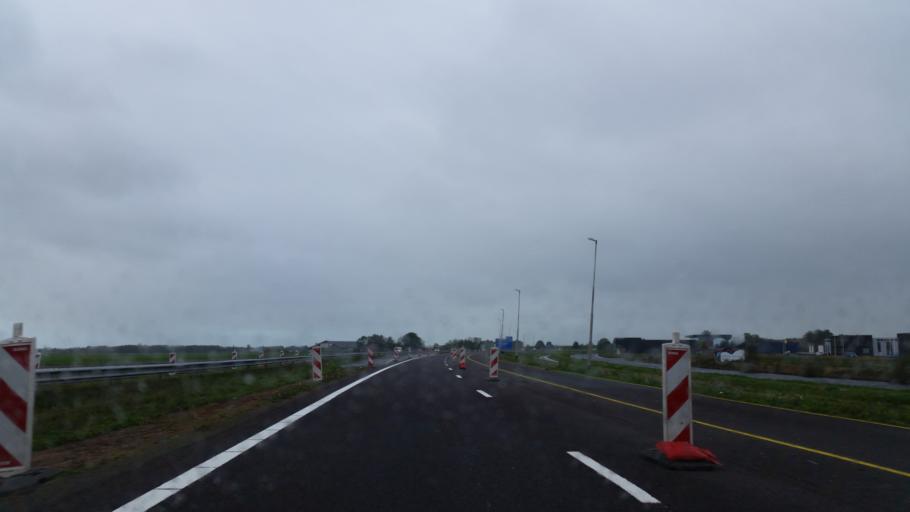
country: NL
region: Friesland
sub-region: Gemeente Skarsterlan
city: Joure
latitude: 52.9562
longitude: 5.7804
